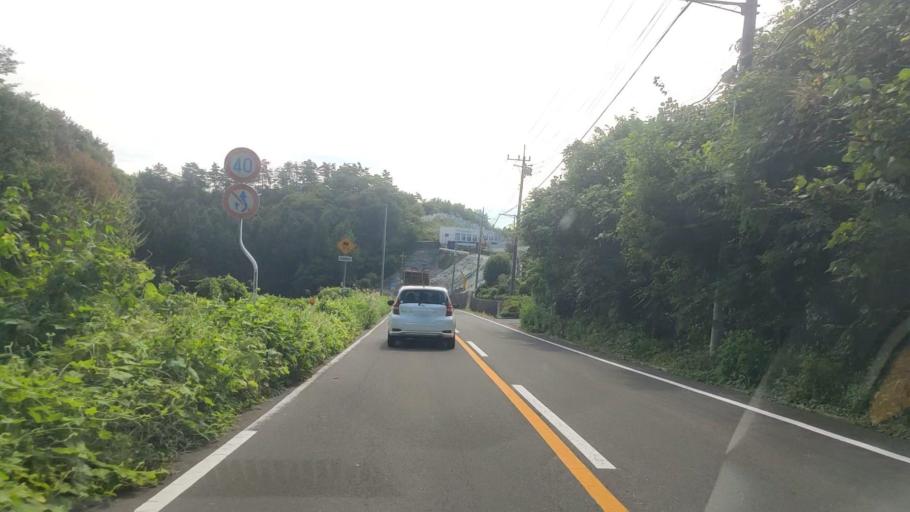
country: JP
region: Gunma
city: Numata
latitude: 36.6278
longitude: 139.0127
